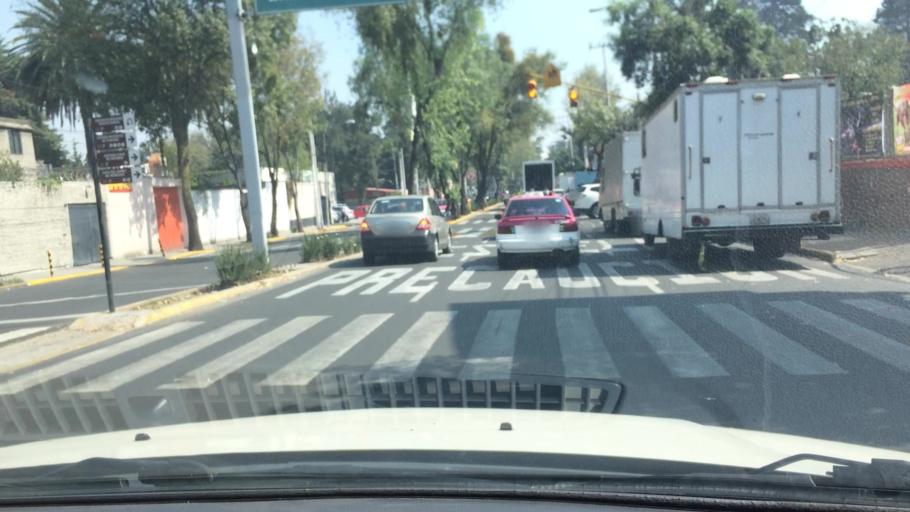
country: MX
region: Mexico City
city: Tlalpan
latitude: 19.2925
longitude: -99.1682
